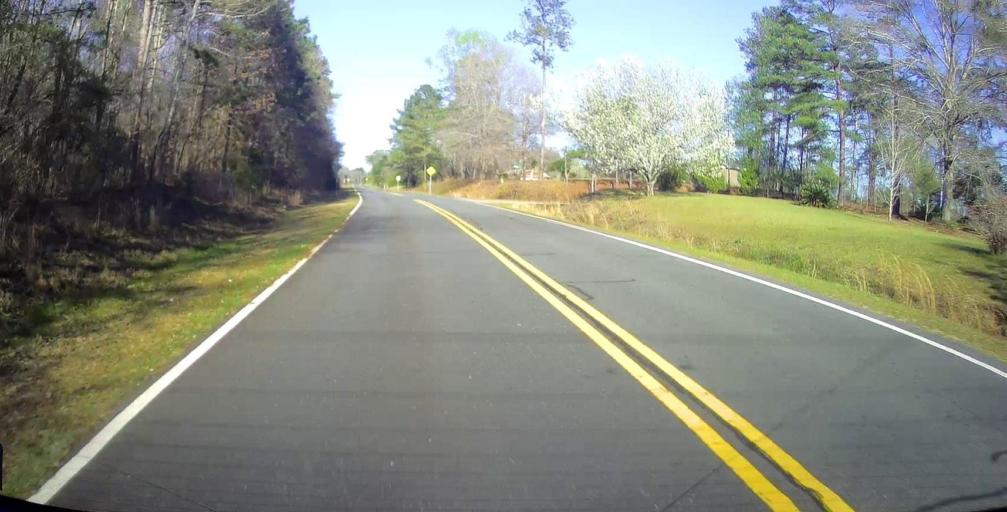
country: US
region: Georgia
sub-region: Peach County
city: Fort Valley
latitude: 32.5211
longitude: -83.9151
